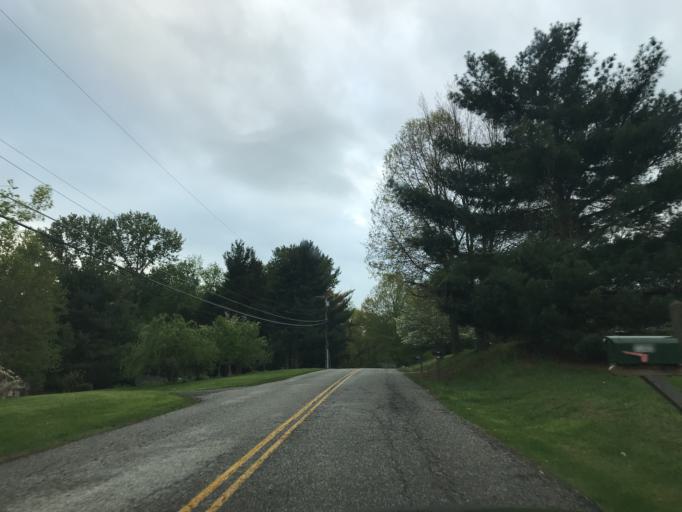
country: US
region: Maryland
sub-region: Harford County
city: Jarrettsville
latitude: 39.6642
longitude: -76.4874
